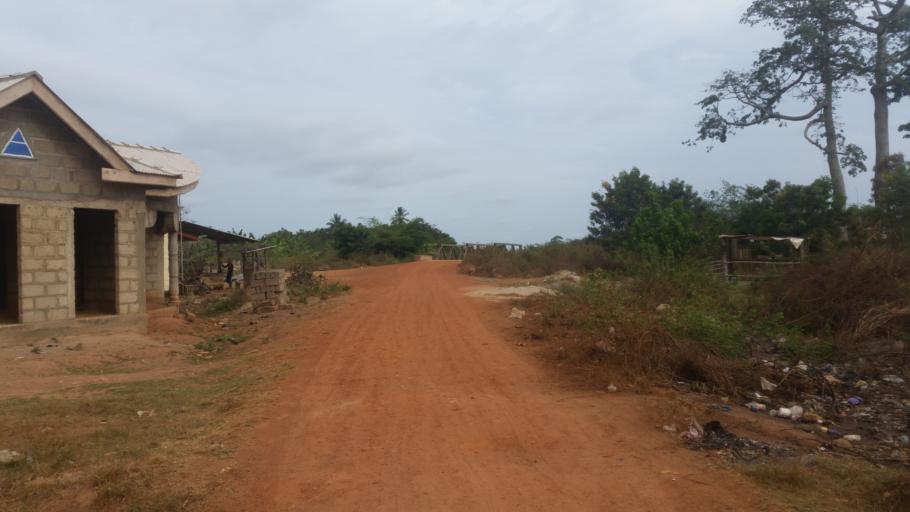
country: GH
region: Central
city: Cape Coast
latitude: 5.1259
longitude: -1.3020
